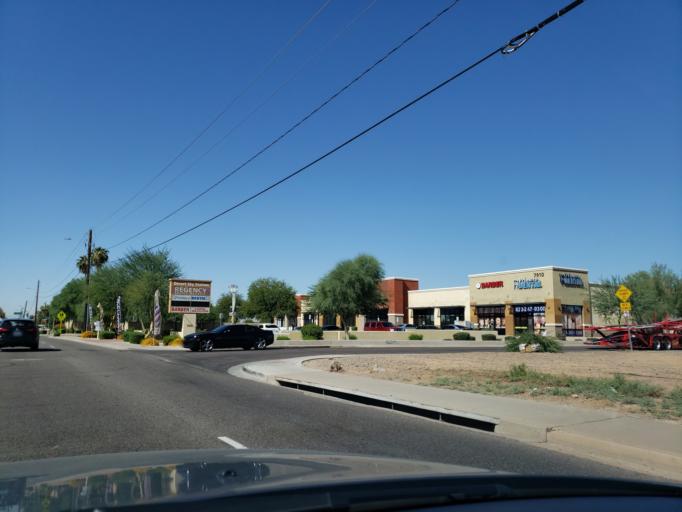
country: US
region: Arizona
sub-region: Maricopa County
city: Tolleson
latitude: 33.4802
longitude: -112.2268
